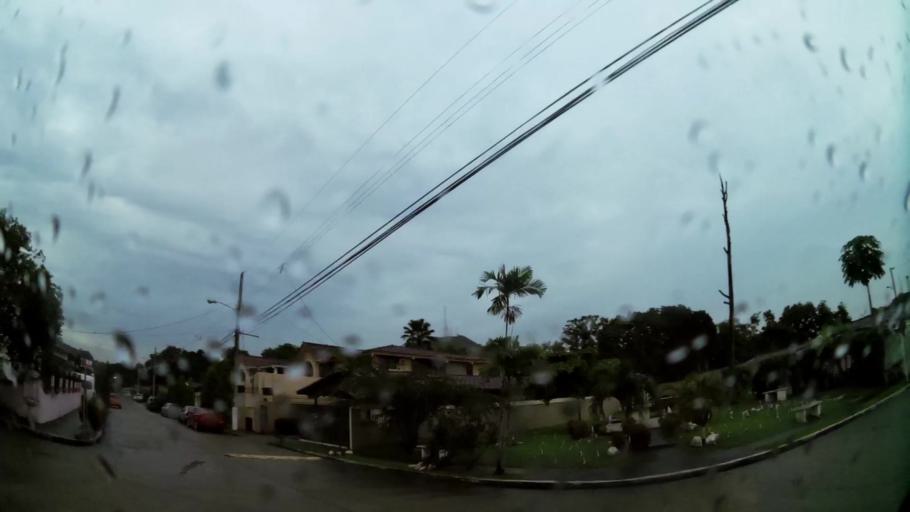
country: PA
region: Panama
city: Las Cumbres
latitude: 9.0428
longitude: -79.5289
